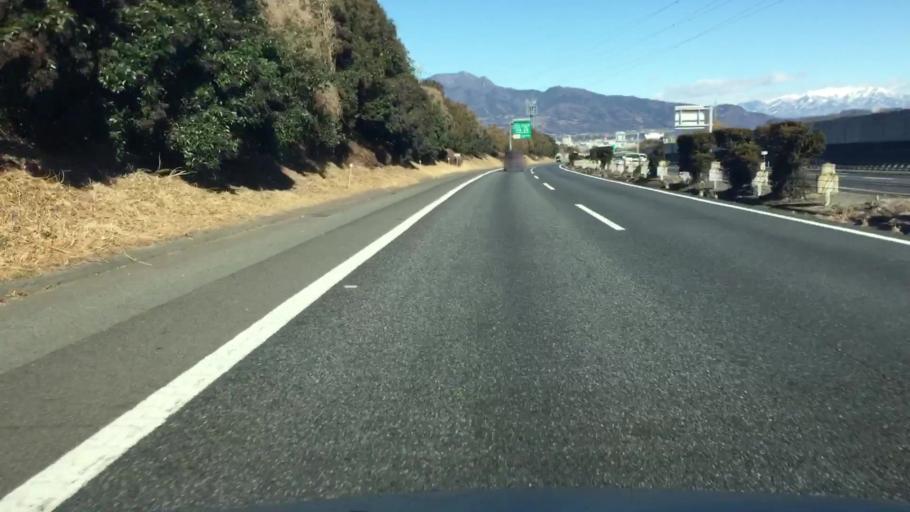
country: JP
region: Gunma
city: Shibukawa
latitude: 36.4638
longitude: 139.0115
